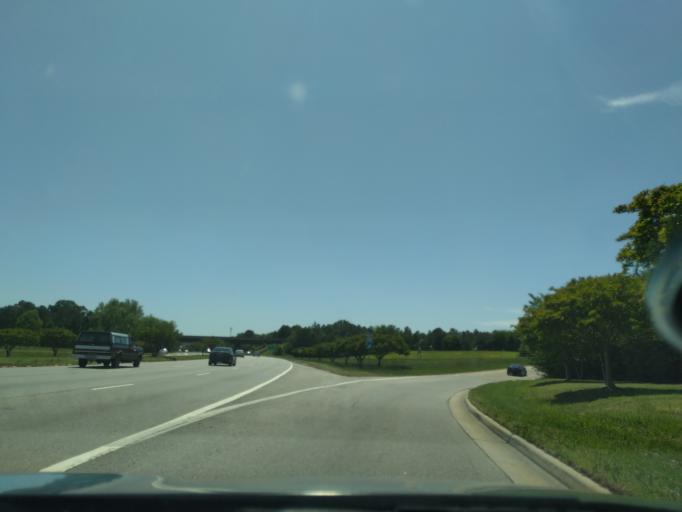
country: US
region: Virginia
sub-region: Prince George County
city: Fort Lee
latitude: 37.2690
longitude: -77.3203
